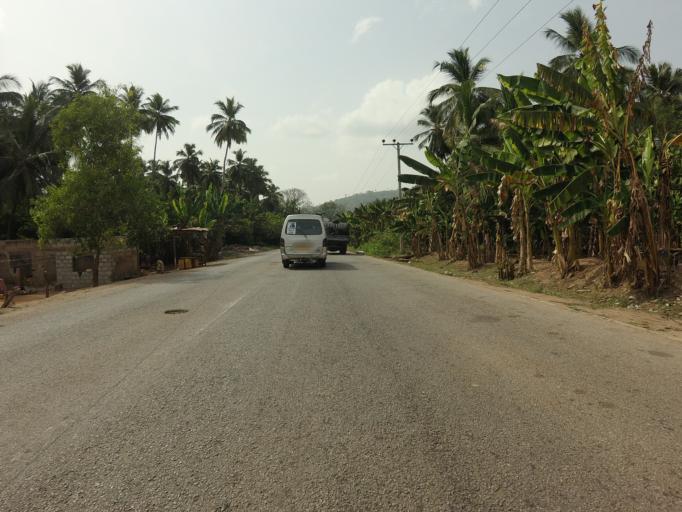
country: GH
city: Akropong
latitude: 6.2918
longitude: 0.1327
